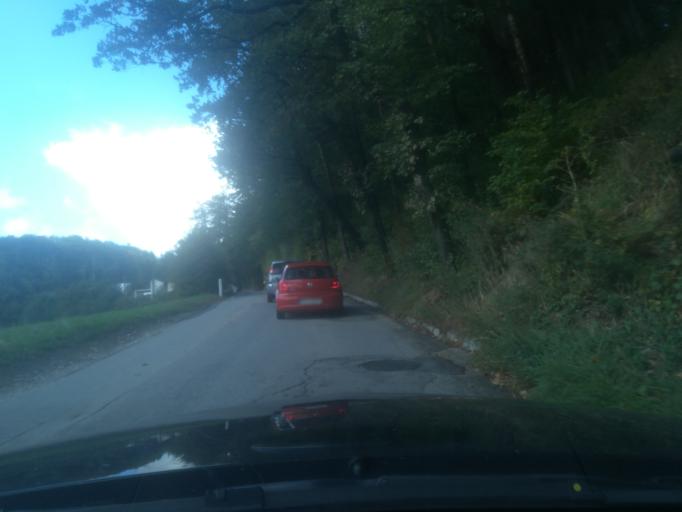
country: AT
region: Upper Austria
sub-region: Linz Stadt
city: Linz
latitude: 48.3395
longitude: 14.2737
